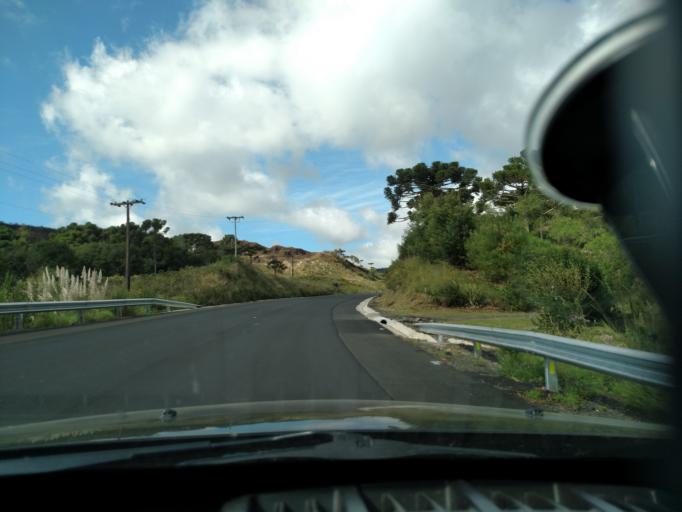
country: BR
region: Santa Catarina
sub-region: Lages
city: Lages
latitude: -27.9392
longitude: -50.0938
